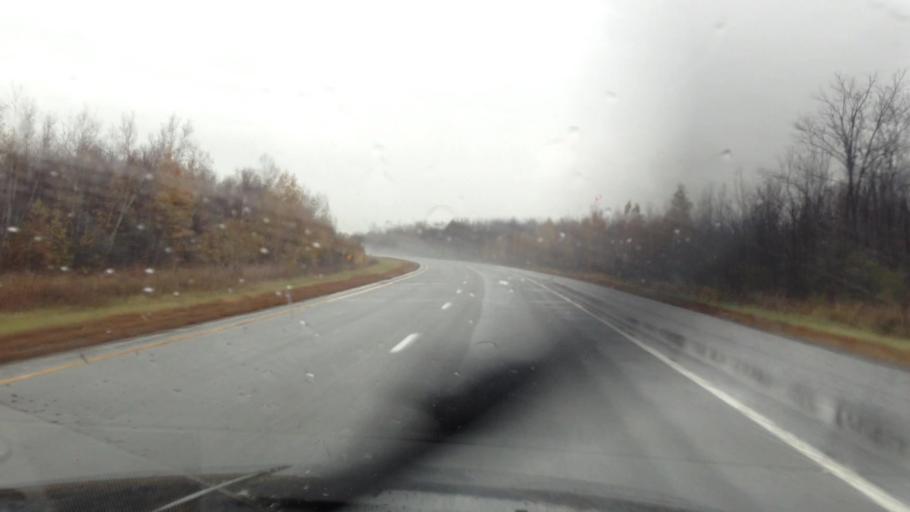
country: CA
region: Ontario
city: Casselman
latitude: 45.3053
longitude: -75.1451
